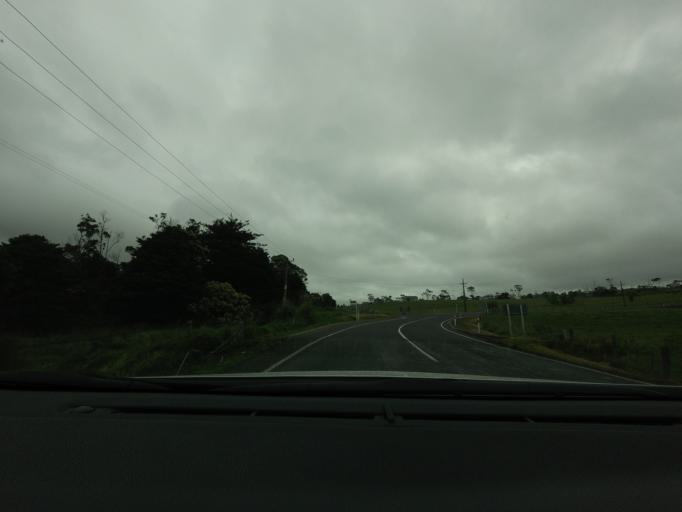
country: NZ
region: Auckland
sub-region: Auckland
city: Wellsford
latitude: -36.2839
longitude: 174.5664
